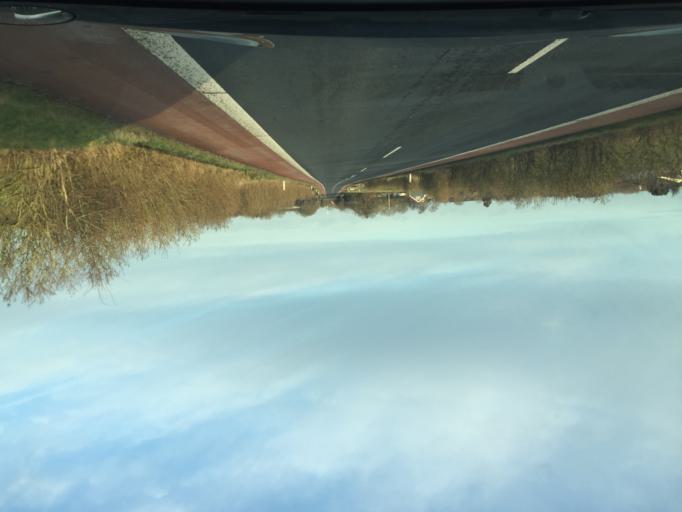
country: DK
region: South Denmark
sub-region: Faaborg-Midtfyn Kommune
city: Arslev
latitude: 55.2890
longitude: 10.4499
